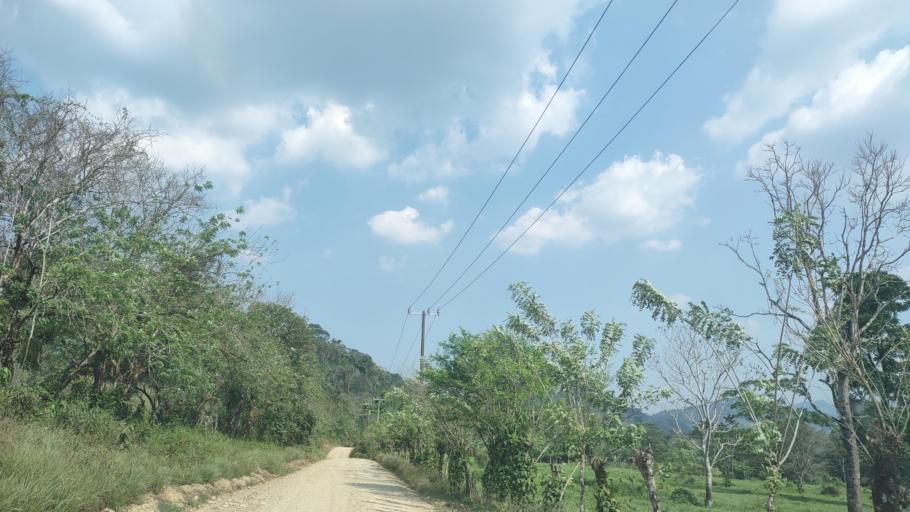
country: MX
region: Chiapas
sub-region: Tecpatan
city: Raudales Malpaso
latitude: 17.3320
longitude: -93.7501
